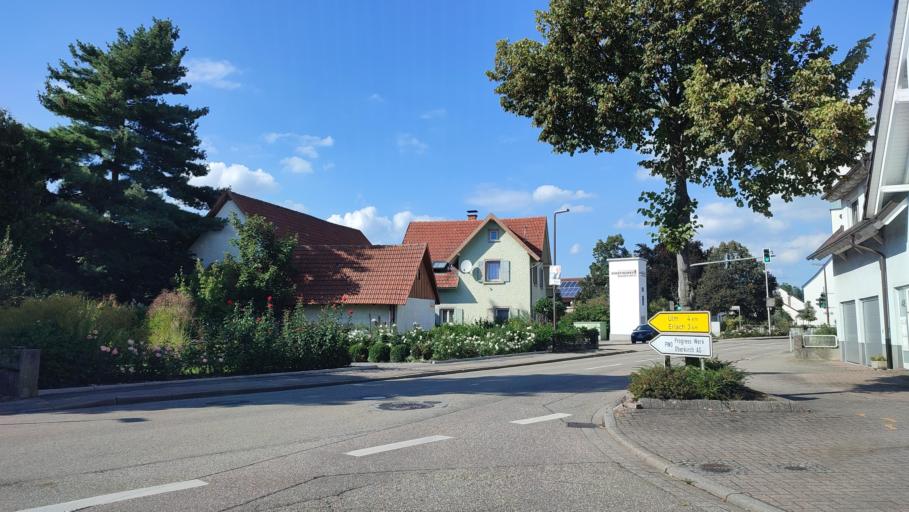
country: DE
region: Baden-Wuerttemberg
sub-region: Freiburg Region
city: Appenweier
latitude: 48.5476
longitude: 8.0173
